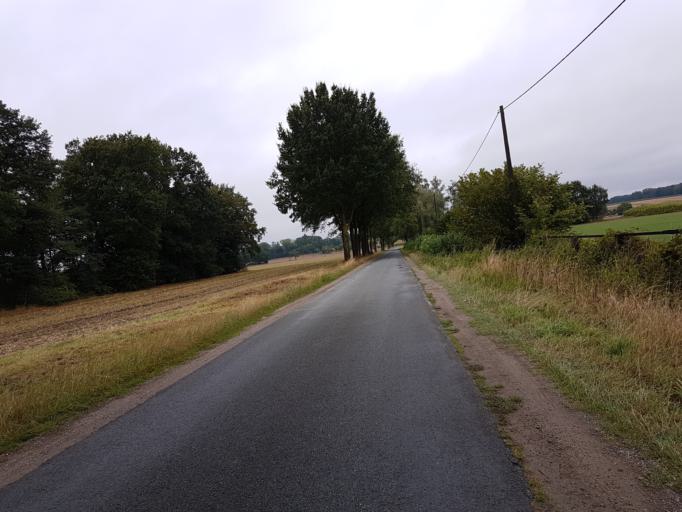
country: DE
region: North Rhine-Westphalia
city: Olfen
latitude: 51.7236
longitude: 7.3853
